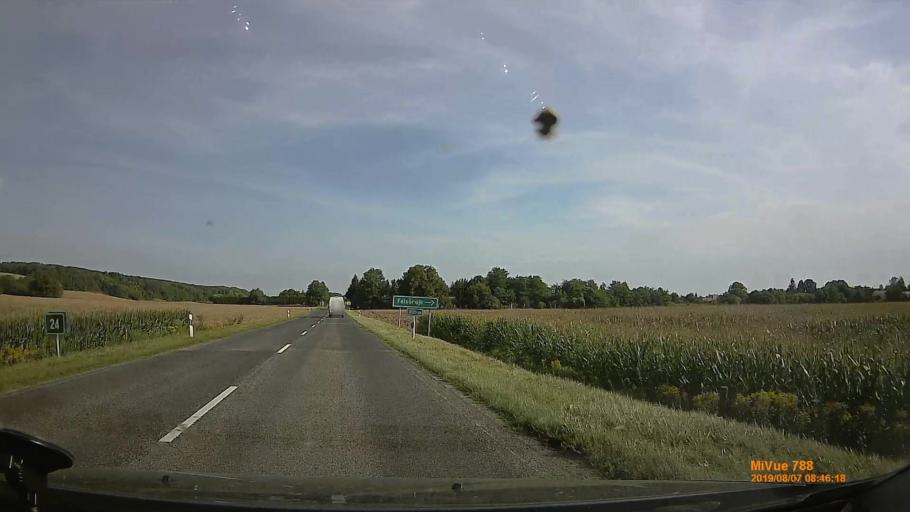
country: HU
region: Zala
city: Pacsa
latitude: 46.6461
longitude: 16.9195
